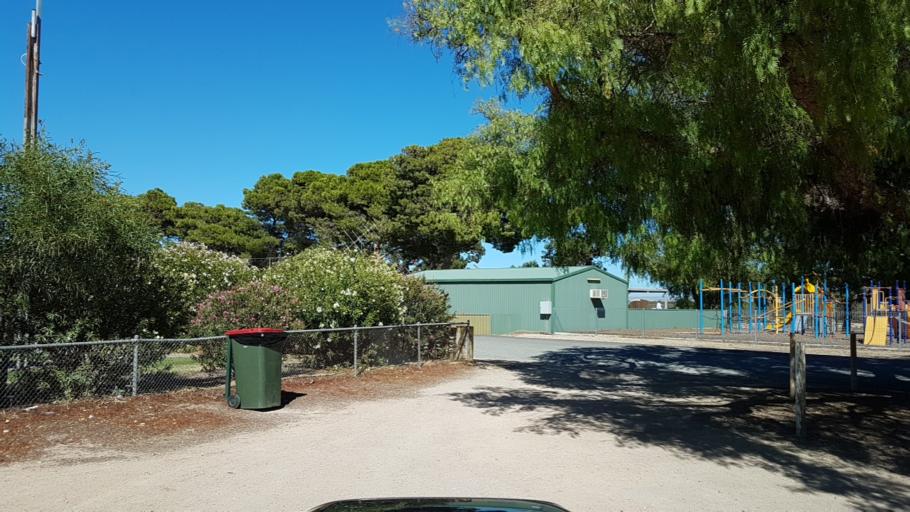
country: AU
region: South Australia
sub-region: Wakefield
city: Balaklava
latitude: -34.1853
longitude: 138.1463
